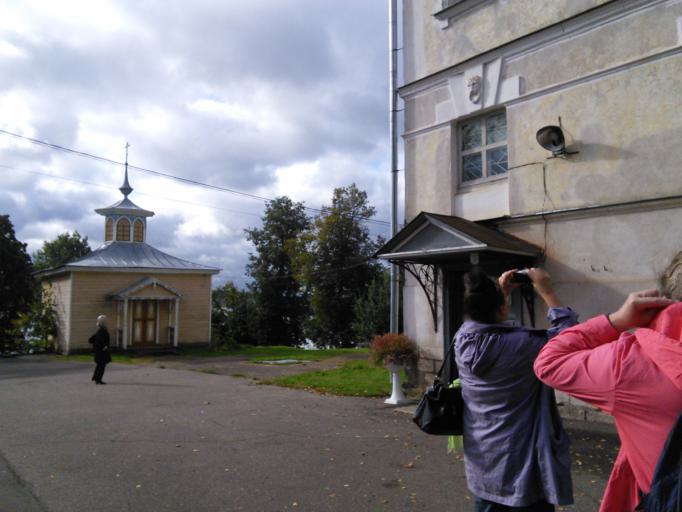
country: RU
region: Jaroslavl
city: Myshkin
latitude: 57.7867
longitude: 38.4567
